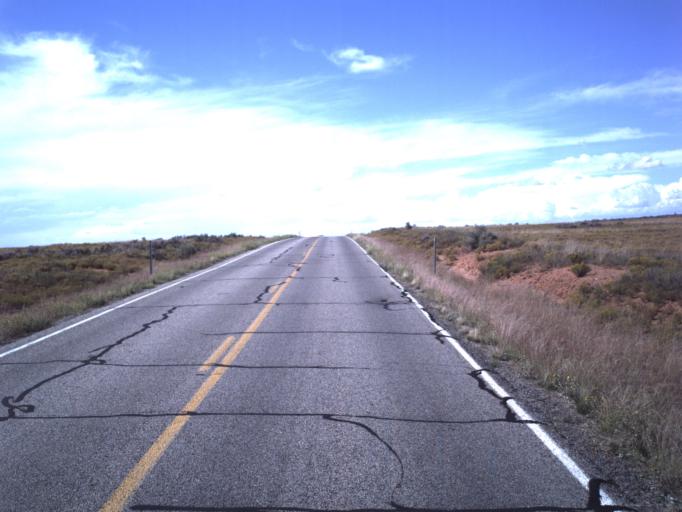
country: US
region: Utah
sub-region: Grand County
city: Moab
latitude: 38.5332
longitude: -109.7527
